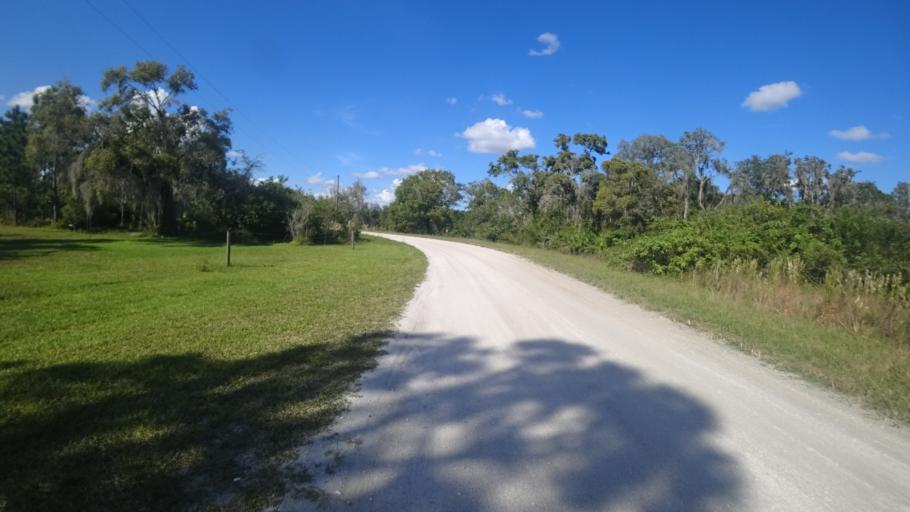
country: US
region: Florida
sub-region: Hardee County
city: Wauchula
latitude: 27.4851
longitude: -82.0565
